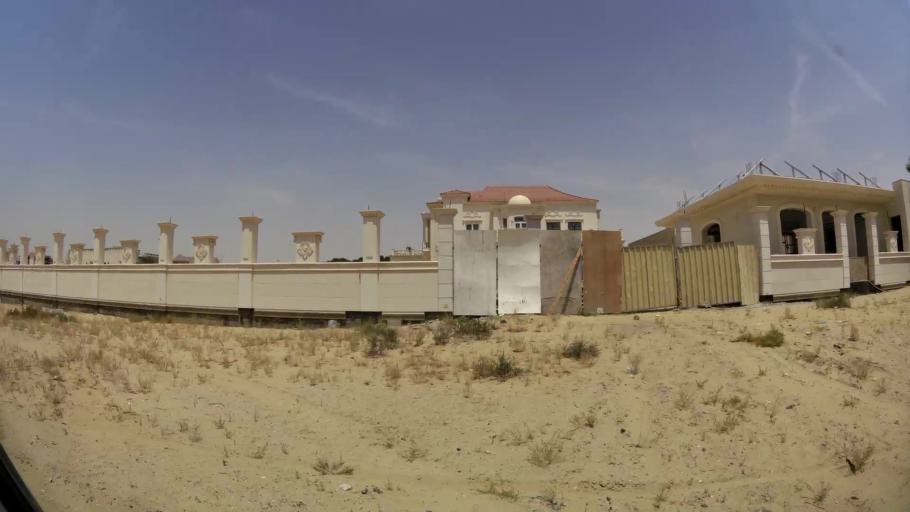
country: AE
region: Ash Shariqah
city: Sharjah
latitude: 25.2384
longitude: 55.4878
